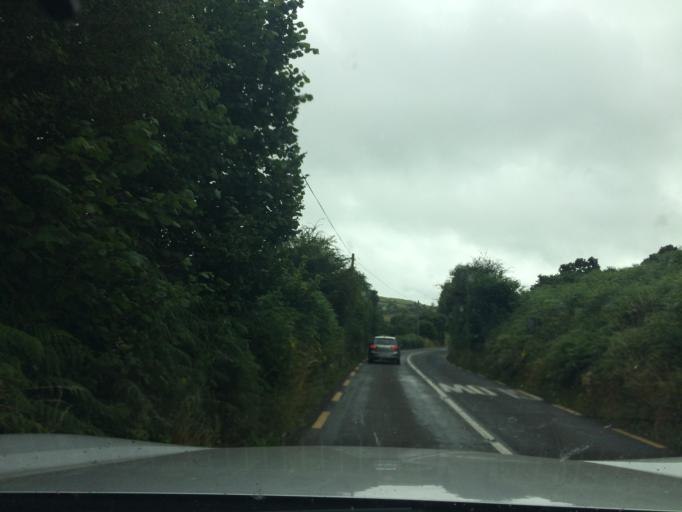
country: IE
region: Munster
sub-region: South Tipperary
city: Cluain Meala
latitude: 52.2494
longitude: -7.7174
